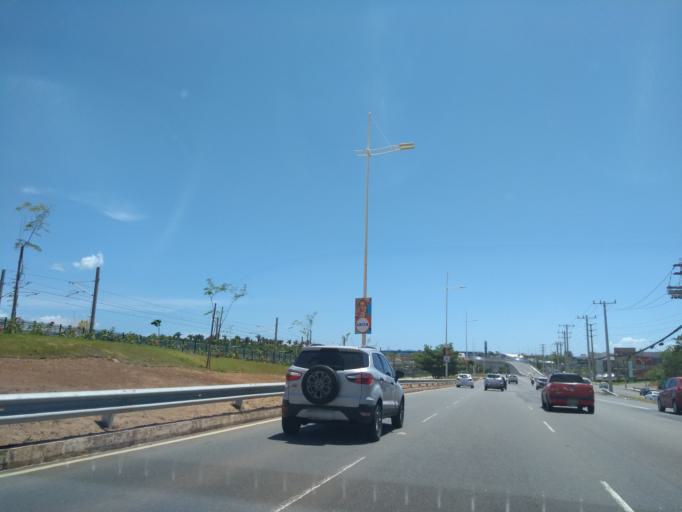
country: BR
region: Bahia
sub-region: Lauro De Freitas
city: Lauro de Freitas
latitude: -12.9378
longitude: -38.4020
